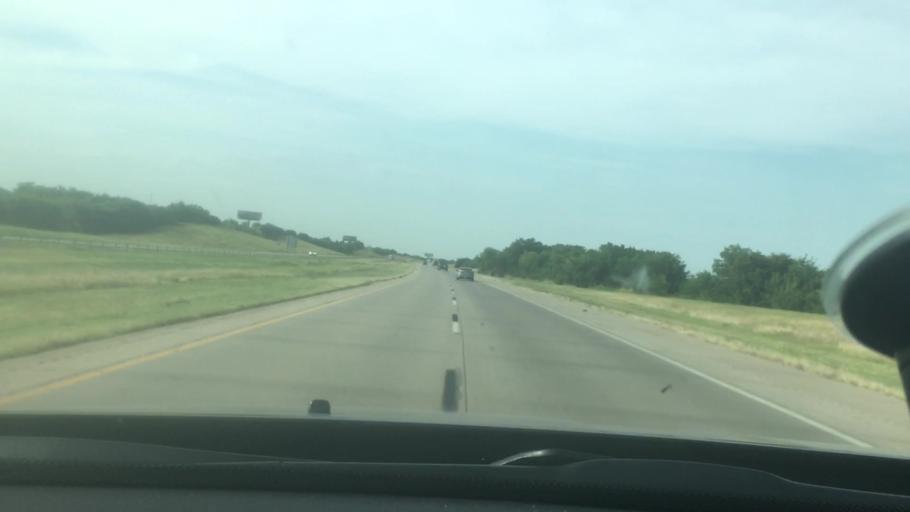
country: US
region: Oklahoma
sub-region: Carter County
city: Ardmore
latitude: 34.3023
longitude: -97.1600
